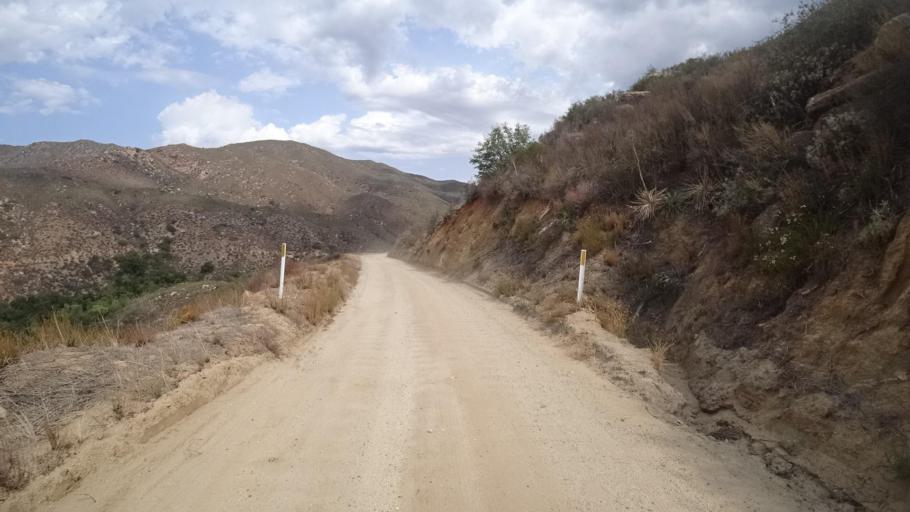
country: US
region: California
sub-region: San Diego County
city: Ramona
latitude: 33.1226
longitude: -116.8058
